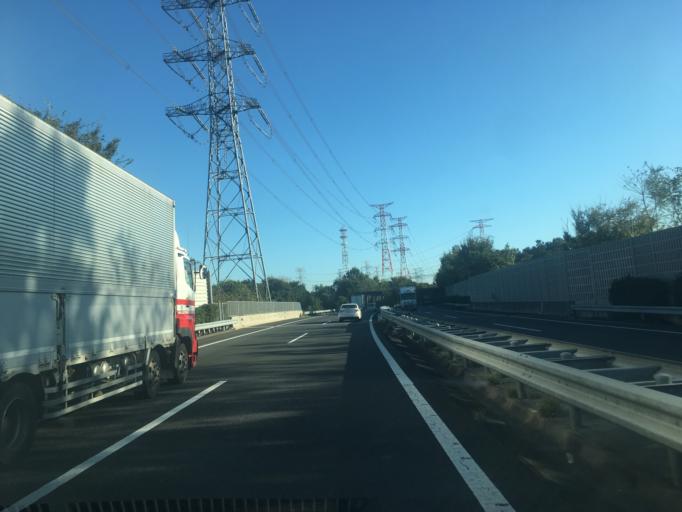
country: JP
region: Saitama
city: Sakado
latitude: 35.9568
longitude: 139.4298
